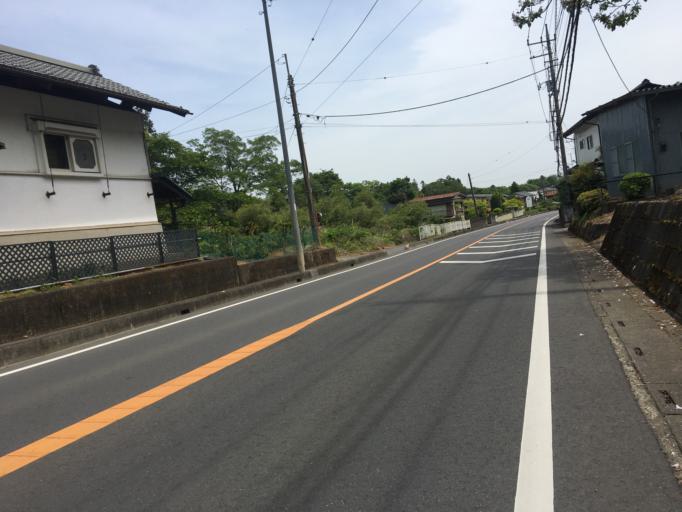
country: JP
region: Saitama
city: Hanno
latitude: 35.8543
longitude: 139.3037
